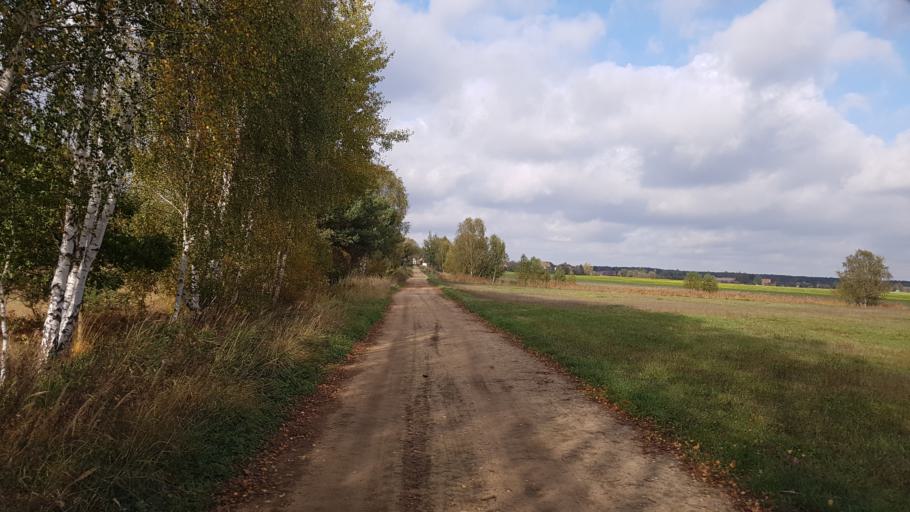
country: DE
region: Brandenburg
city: Schonborn
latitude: 51.5863
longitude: 13.4930
